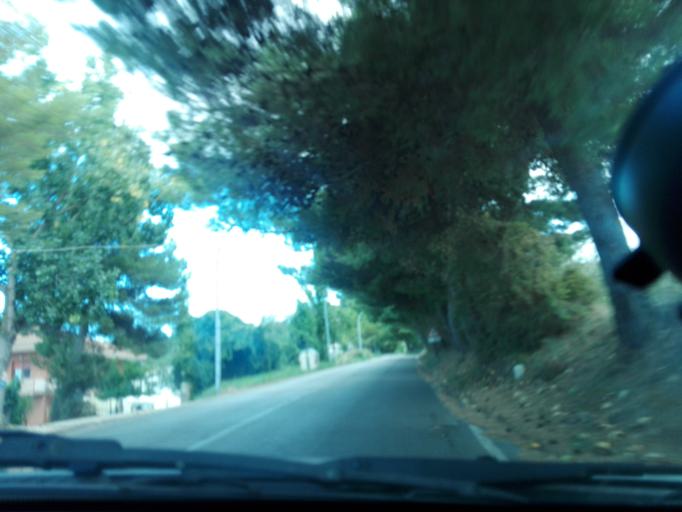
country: IT
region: Abruzzo
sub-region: Provincia di Pescara
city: Montesilvano Marina
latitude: 42.4970
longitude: 14.1423
